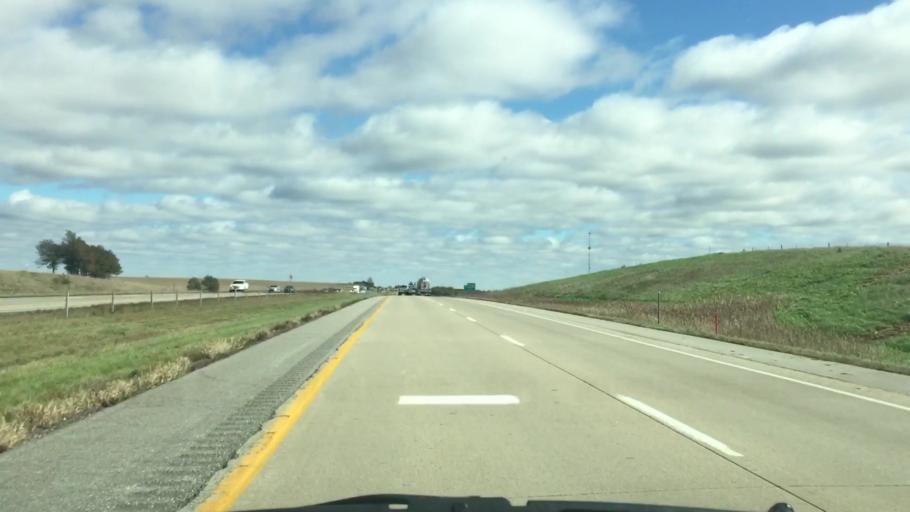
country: US
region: Iowa
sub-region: Poweshiek County
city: Brooklyn
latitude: 41.6949
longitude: -92.4735
